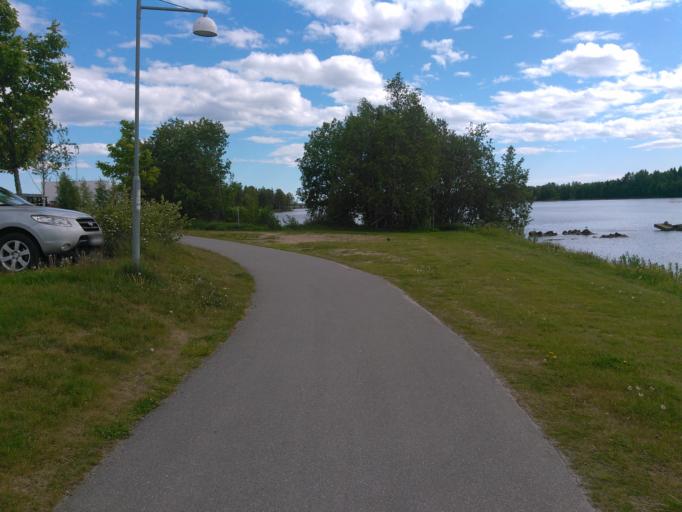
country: SE
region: Vaesterbotten
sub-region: Umea Kommun
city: Umea
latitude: 63.7967
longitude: 20.3012
